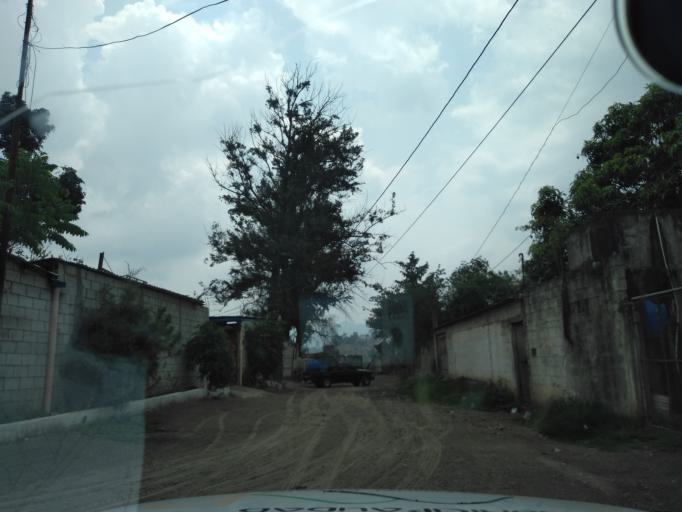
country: GT
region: Guatemala
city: Petapa
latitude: 14.5109
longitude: -90.5539
